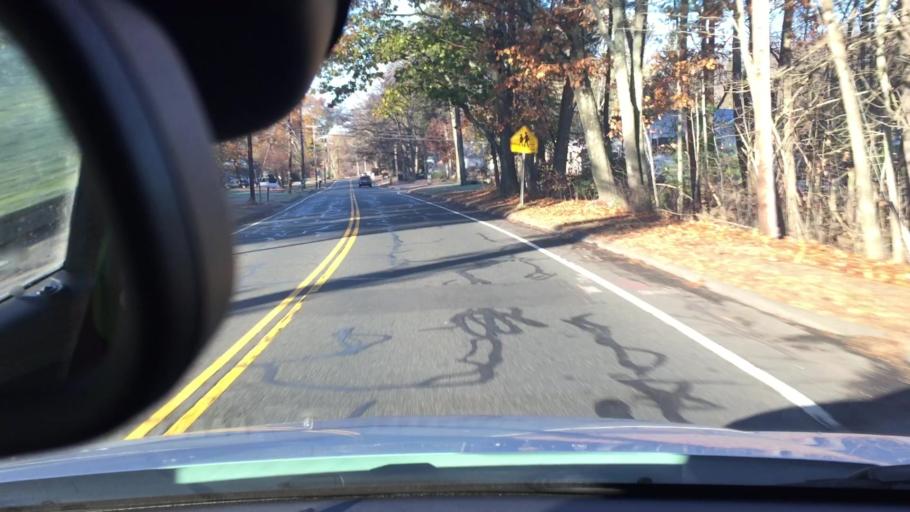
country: US
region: Massachusetts
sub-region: Hampden County
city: Ludlow
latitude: 42.1596
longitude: -72.4428
